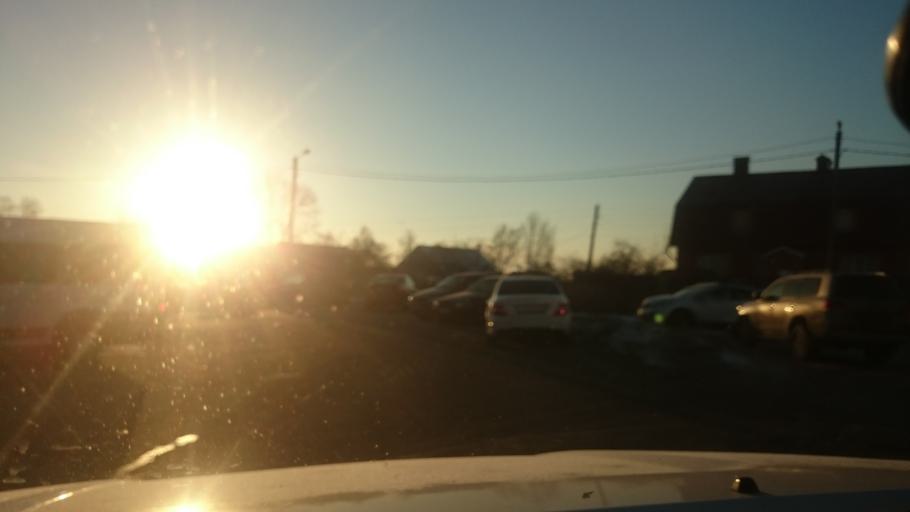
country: RU
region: Tula
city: Tula
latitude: 54.2032
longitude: 37.6999
